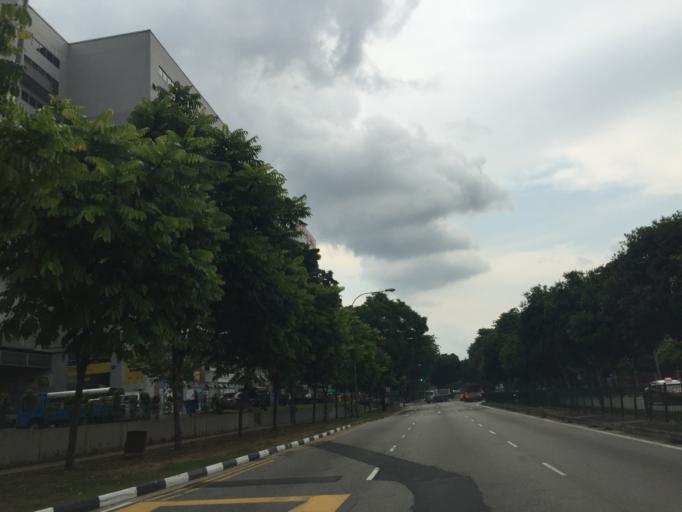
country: MY
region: Johor
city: Johor Bahru
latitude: 1.3336
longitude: 103.6966
